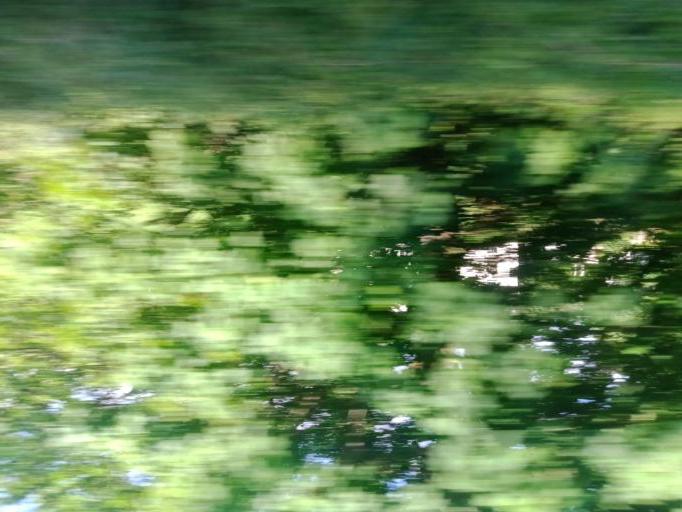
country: GB
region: Wales
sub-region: Gwynedd
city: Aber
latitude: 53.2383
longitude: -4.0238
